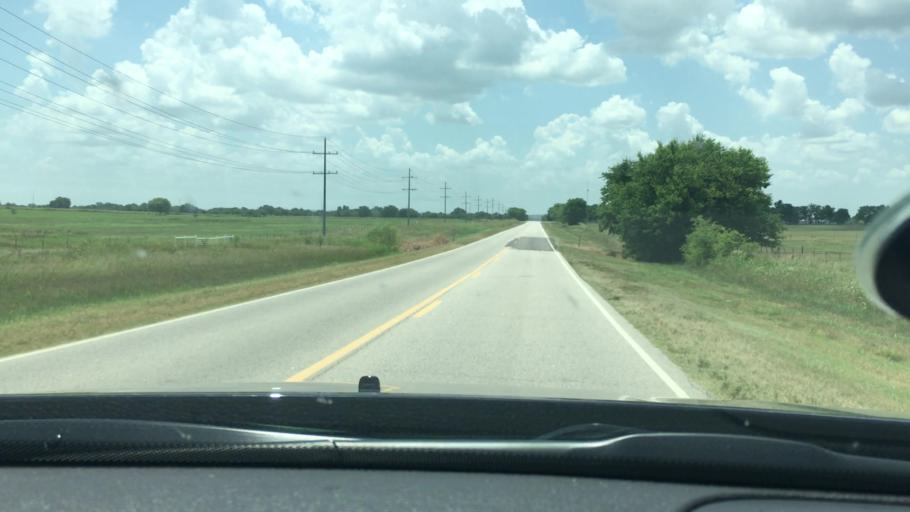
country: US
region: Oklahoma
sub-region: Pontotoc County
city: Ada
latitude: 34.6704
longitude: -96.6349
